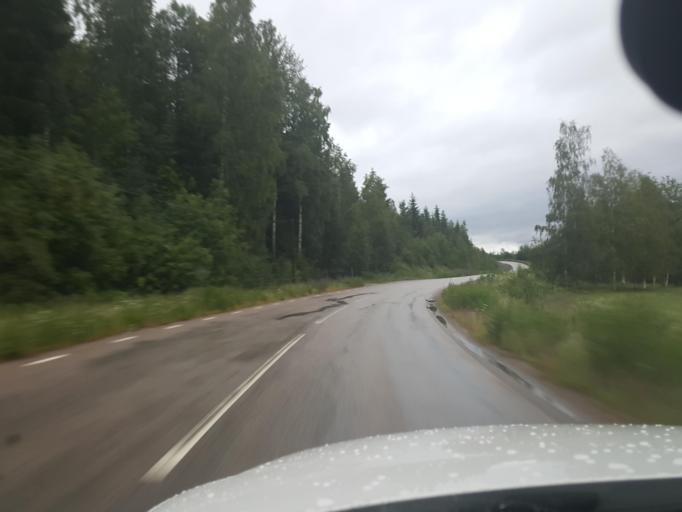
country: SE
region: Gaevleborg
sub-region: Bollnas Kommun
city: Kilafors
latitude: 61.2514
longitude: 16.5949
